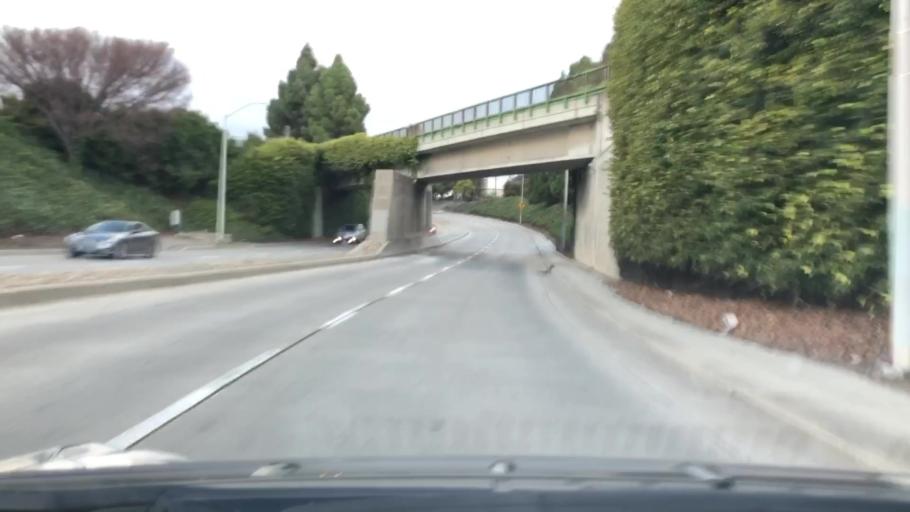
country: US
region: California
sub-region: Santa Clara County
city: Santa Clara
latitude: 37.3806
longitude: -121.9495
